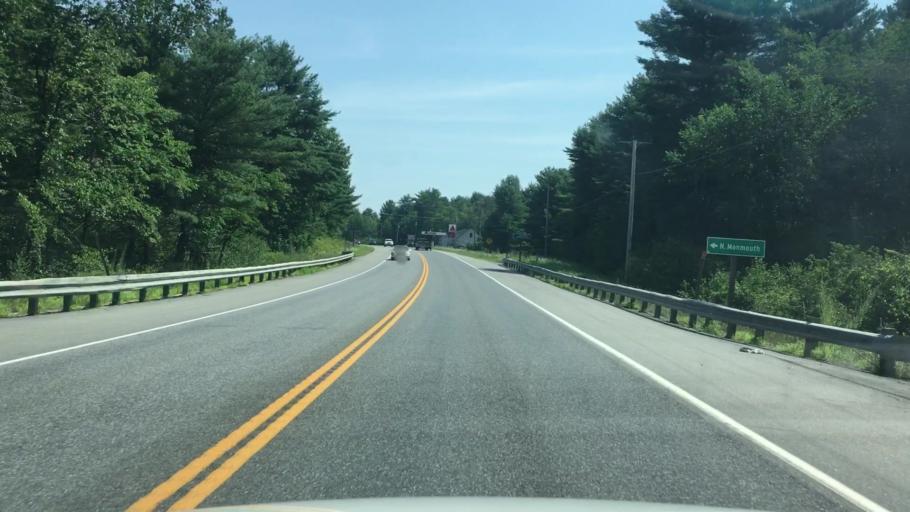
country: US
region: Maine
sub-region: Kennebec County
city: Monmouth
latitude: 44.2687
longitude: -70.0211
